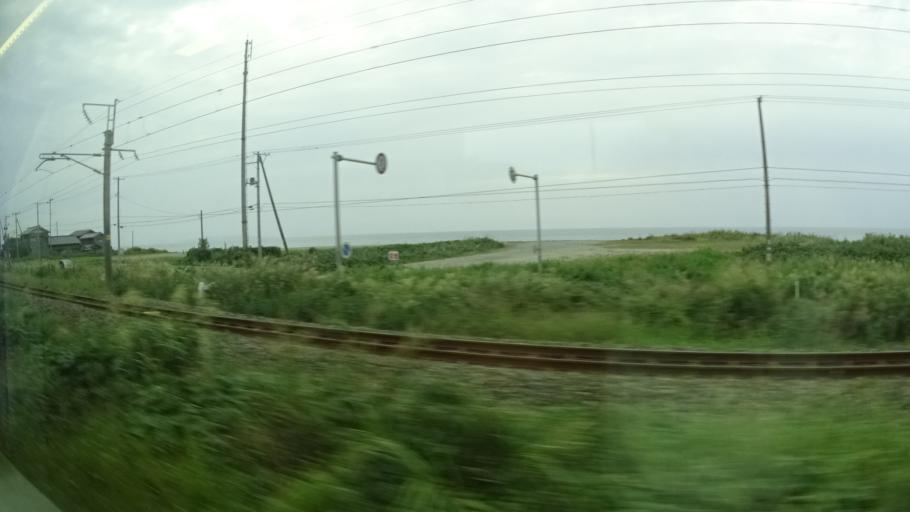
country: JP
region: Niigata
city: Murakami
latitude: 38.5334
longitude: 139.5454
